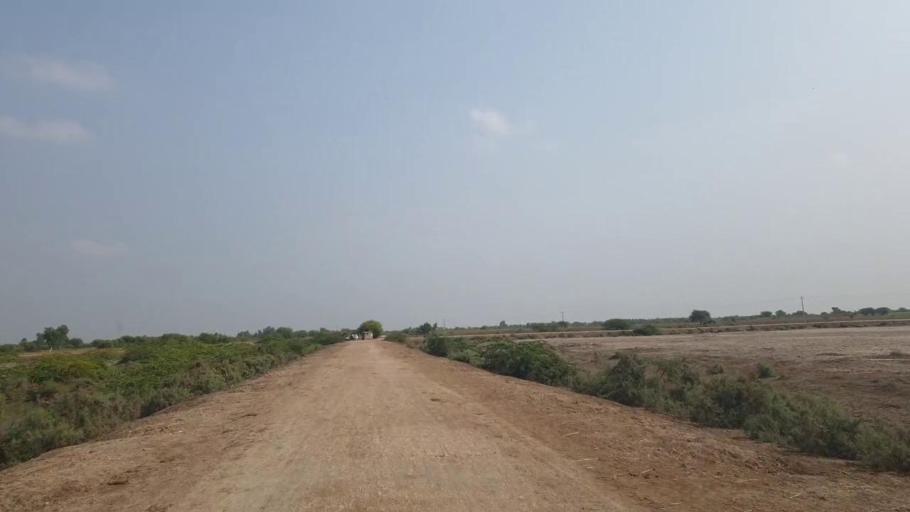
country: PK
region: Sindh
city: Badin
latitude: 24.5475
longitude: 68.7177
